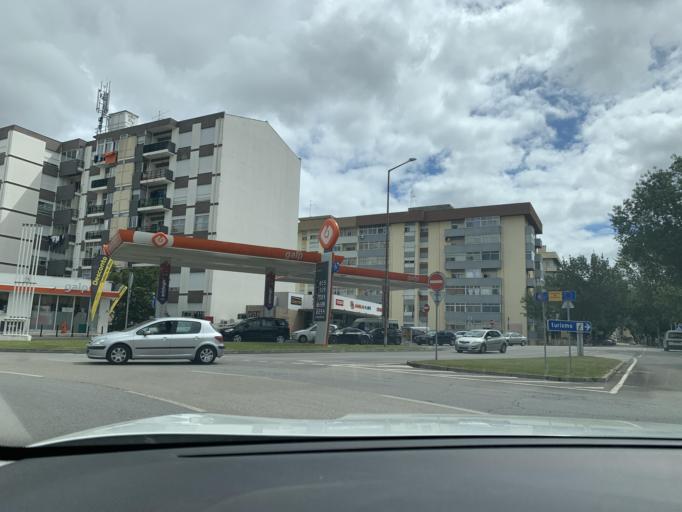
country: PT
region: Viseu
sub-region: Viseu
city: Viseu
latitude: 40.6593
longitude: -7.9232
